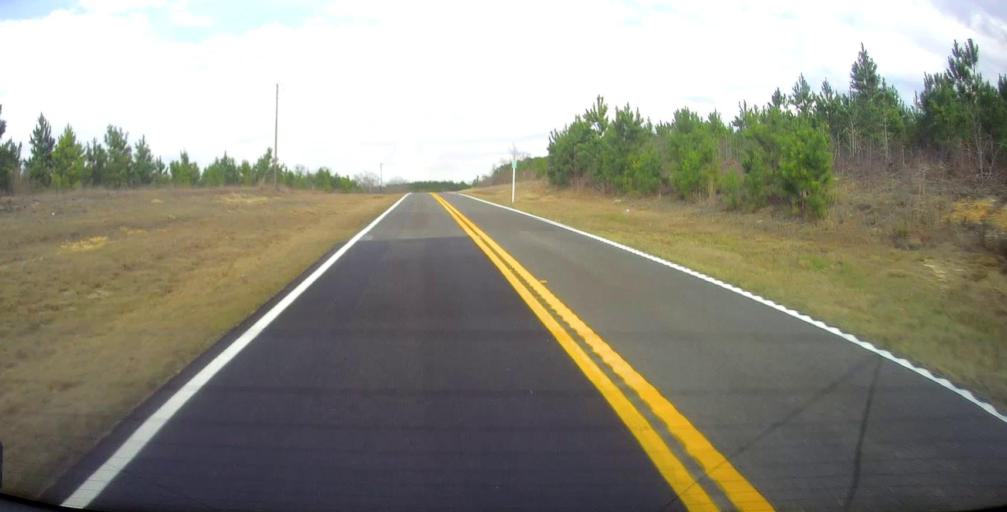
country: US
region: Georgia
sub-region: Marion County
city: Buena Vista
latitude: 32.4500
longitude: -84.4552
